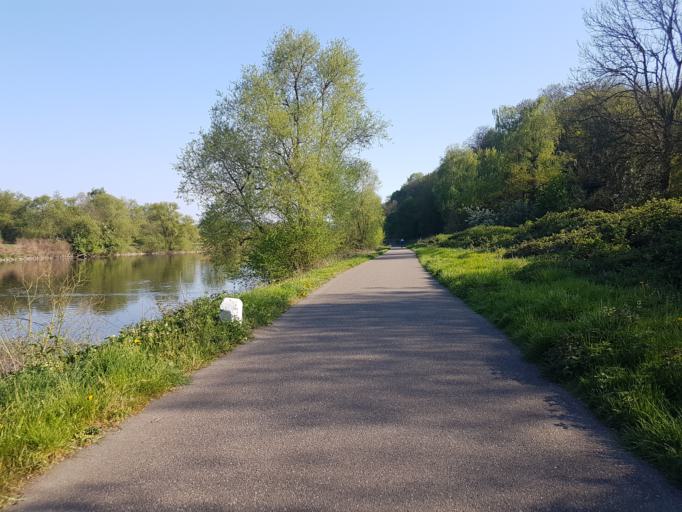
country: DE
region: North Rhine-Westphalia
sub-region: Regierungsbezirk Dusseldorf
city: Essen
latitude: 51.4363
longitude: 7.0845
